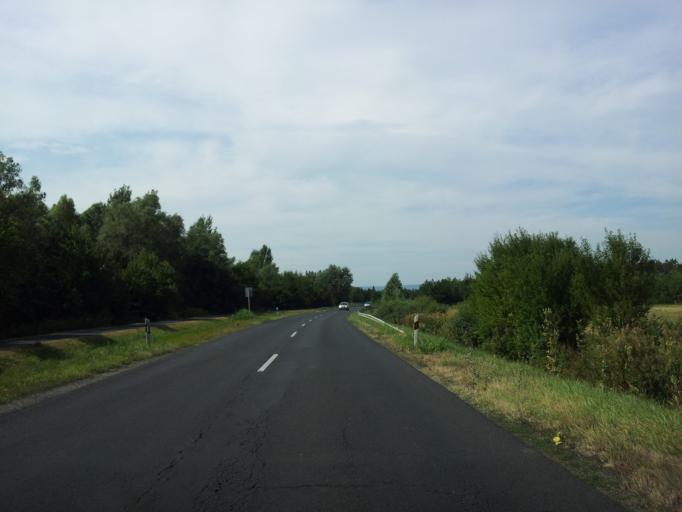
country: HU
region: Veszprem
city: Tapolca
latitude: 46.8845
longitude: 17.4854
